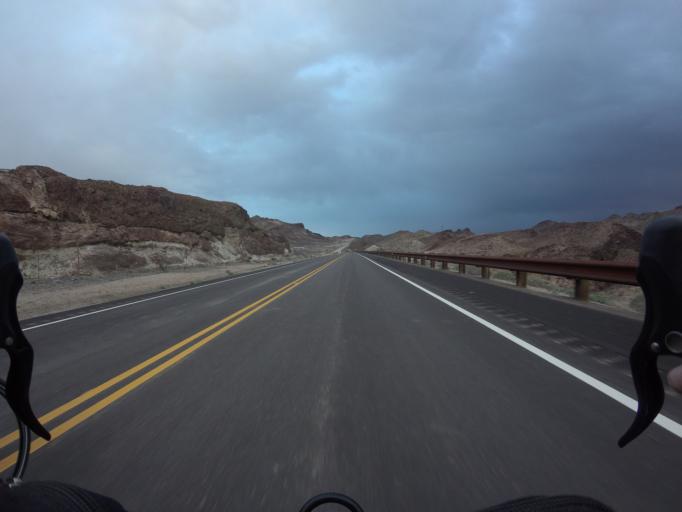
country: US
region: Nevada
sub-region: Clark County
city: Boulder City
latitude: 36.0044
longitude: -114.7251
